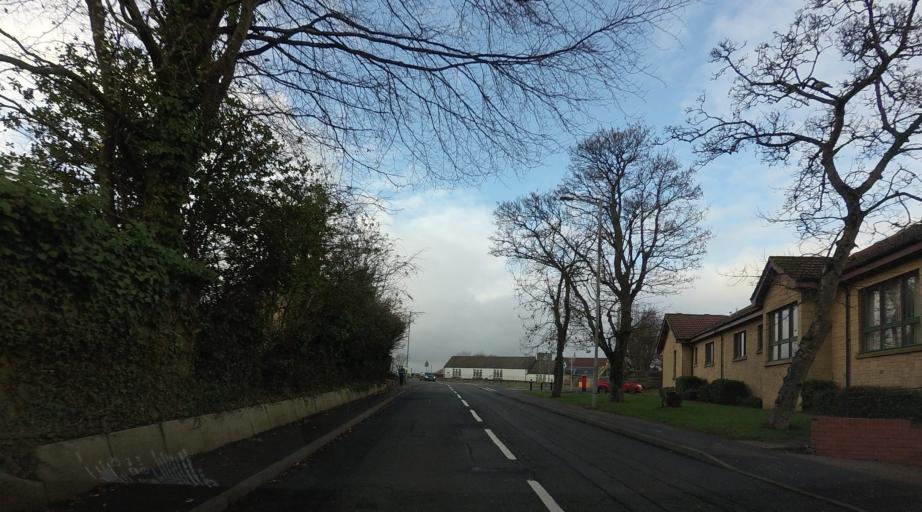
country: GB
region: Scotland
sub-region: Falkirk
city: Polmont
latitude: 55.9779
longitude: -3.7132
